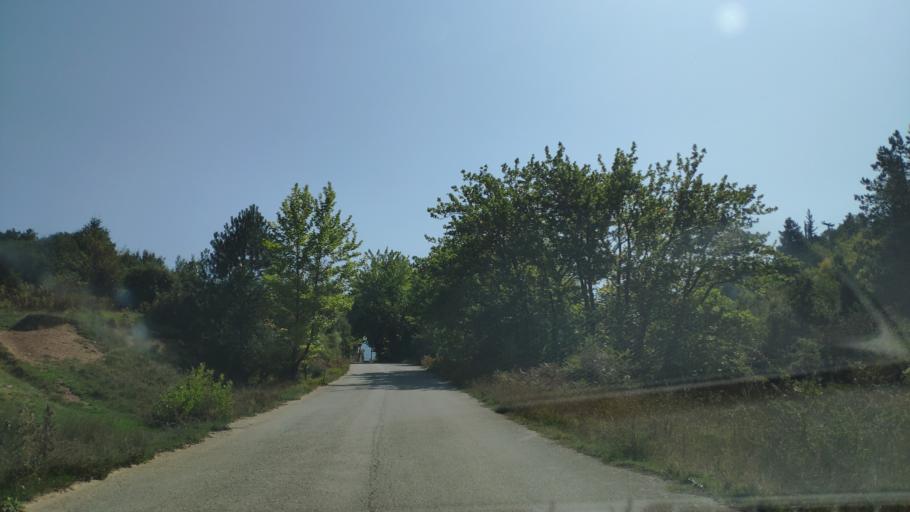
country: GR
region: West Greece
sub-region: Nomos Achaias
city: Kalavryta
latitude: 37.9226
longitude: 22.2943
